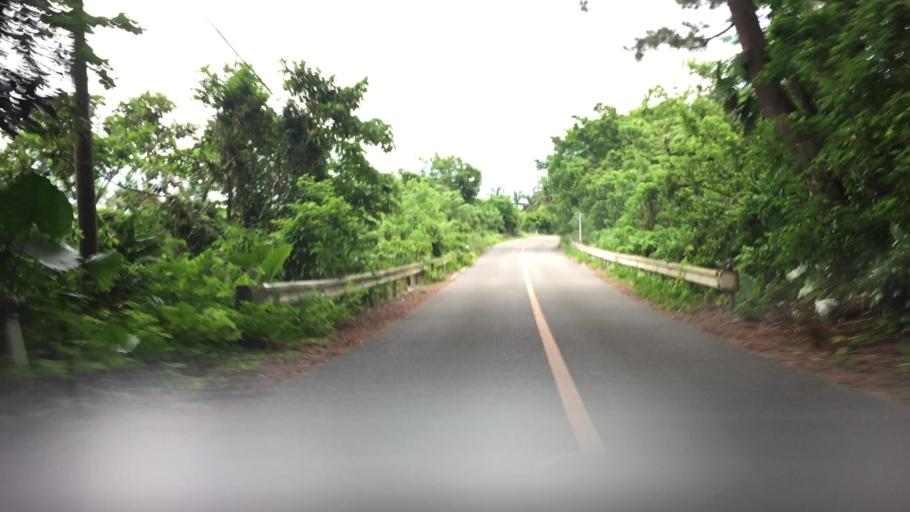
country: JP
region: Okinawa
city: Ishigaki
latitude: 24.3768
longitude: 124.1312
